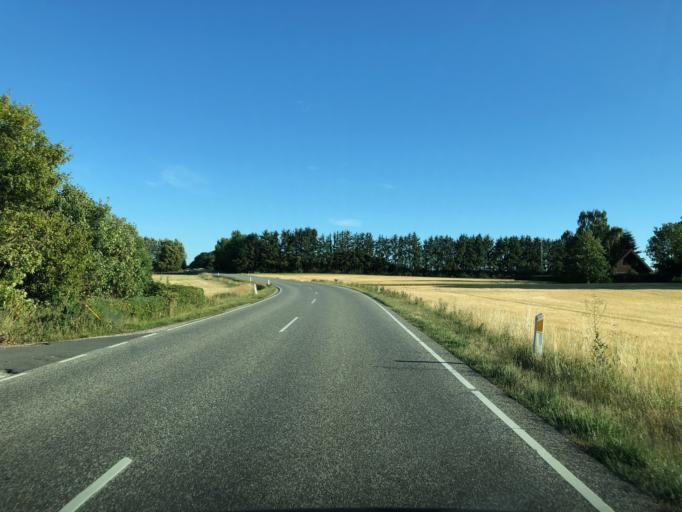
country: DK
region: Central Jutland
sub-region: Skanderborg Kommune
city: Stilling
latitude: 56.0836
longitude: 9.9716
